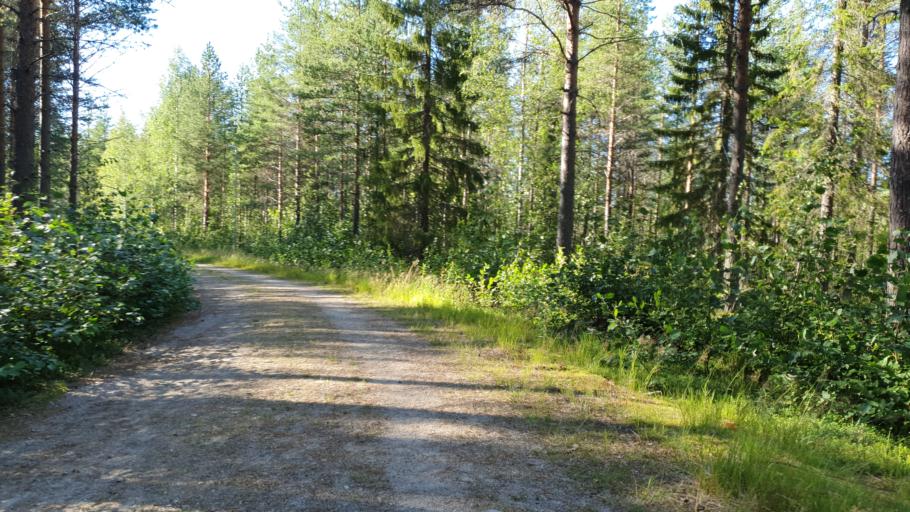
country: FI
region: Kainuu
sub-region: Kehys-Kainuu
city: Kuhmo
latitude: 64.1136
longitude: 29.5025
